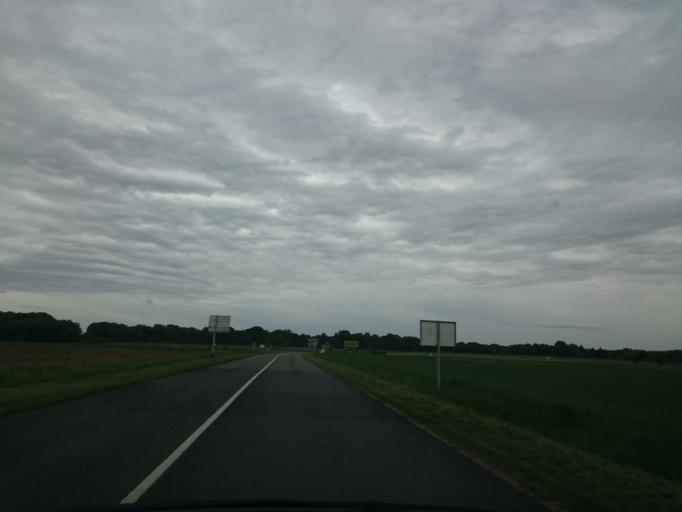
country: FR
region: Centre
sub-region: Departement du Loir-et-Cher
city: Muides-sur-Loire
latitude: 47.6623
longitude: 1.5343
